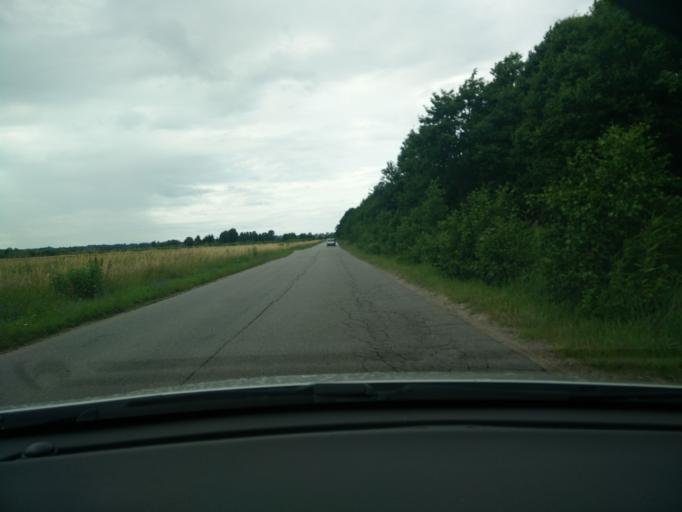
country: PL
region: Pomeranian Voivodeship
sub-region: Powiat pucki
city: Kosakowo
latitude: 54.6105
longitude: 18.4509
